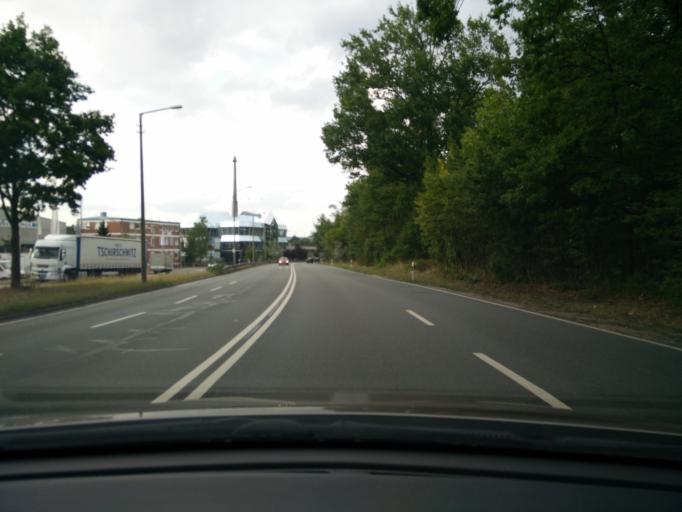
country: DE
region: Bavaria
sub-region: Regierungsbezirk Mittelfranken
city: Wendelstein
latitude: 49.4013
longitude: 11.1277
